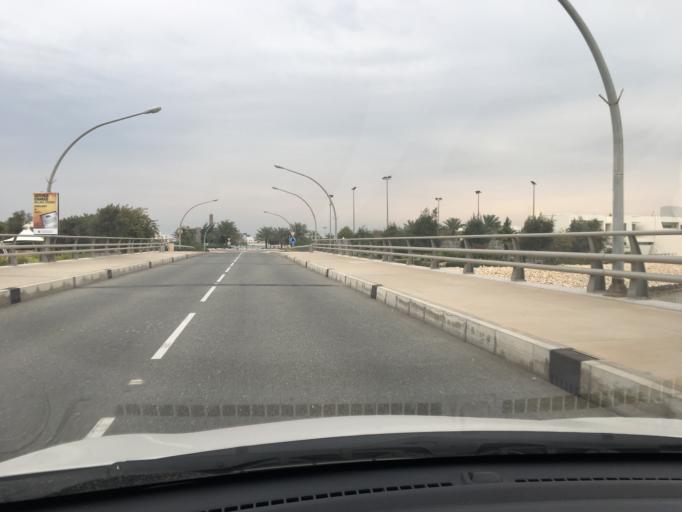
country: BH
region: Central Governorate
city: Dar Kulayb
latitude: 25.8453
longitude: 50.6168
